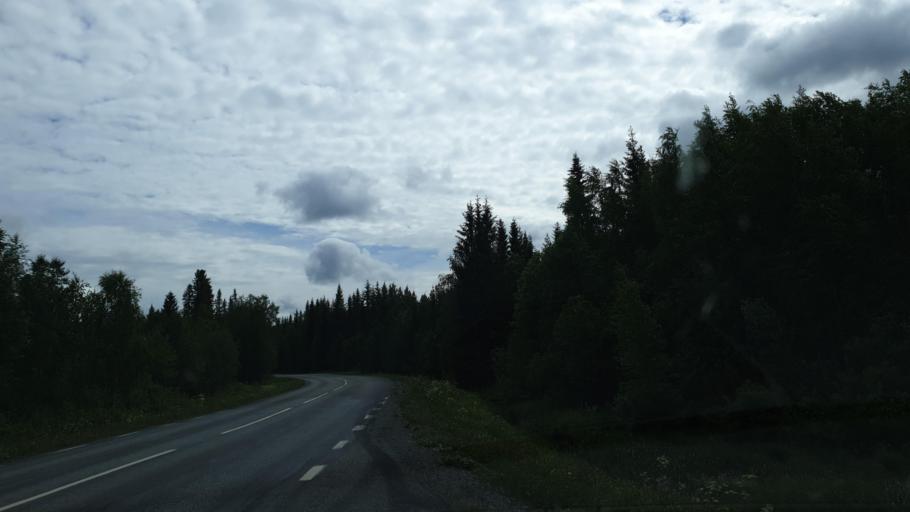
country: SE
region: Vaesterbotten
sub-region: Vilhelmina Kommun
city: Sjoberg
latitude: 64.6734
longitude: 16.2932
